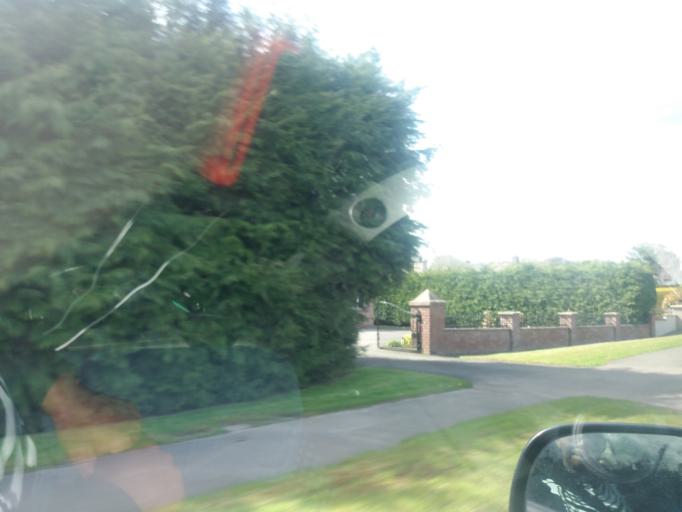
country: GB
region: Northern Ireland
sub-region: Fermanagh District
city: Enniskillen
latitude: 54.3580
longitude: -7.6709
